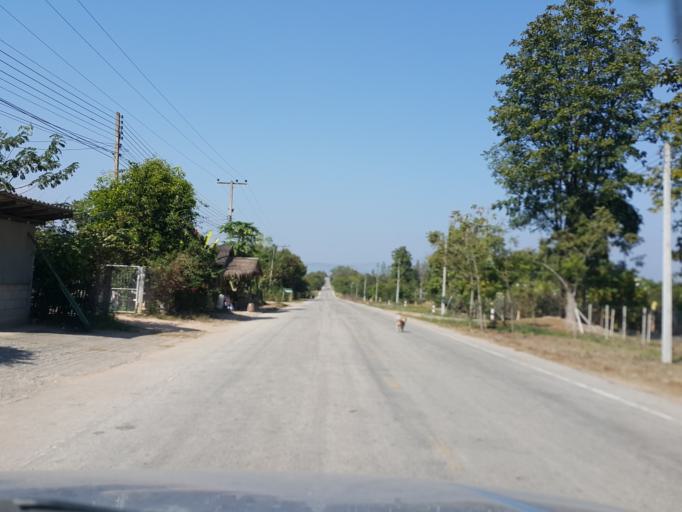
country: TH
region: Chiang Mai
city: Doi Lo
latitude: 18.5356
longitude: 98.7972
